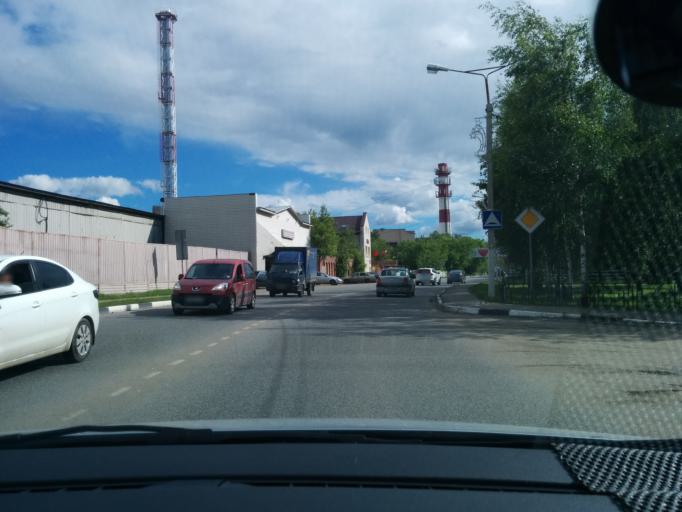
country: RU
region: Moskovskaya
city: Lobnya
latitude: 56.0188
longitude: 37.4725
